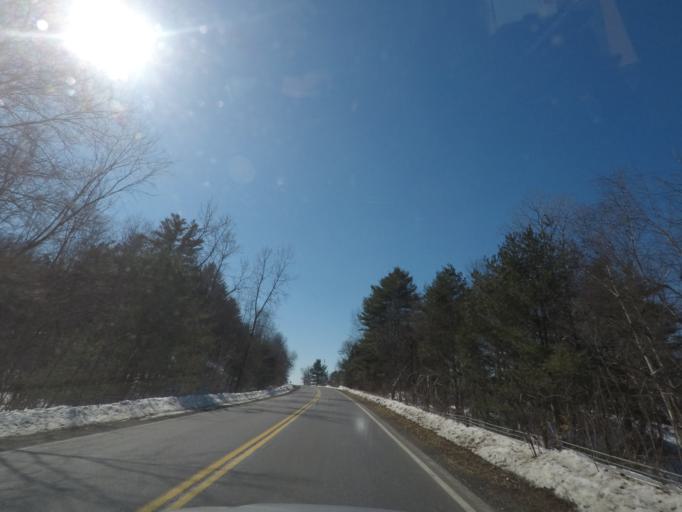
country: US
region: New York
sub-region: Saratoga County
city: Stillwater
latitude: 42.9798
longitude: -73.6099
